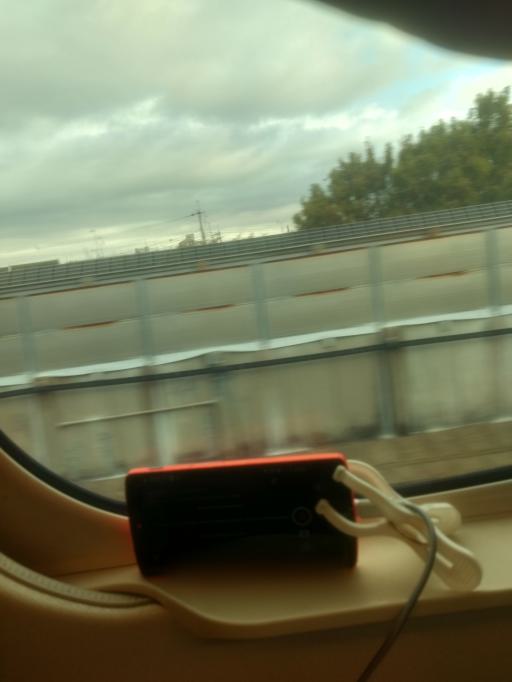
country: JP
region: Hyogo
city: Akashi
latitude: 34.6658
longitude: 134.9760
